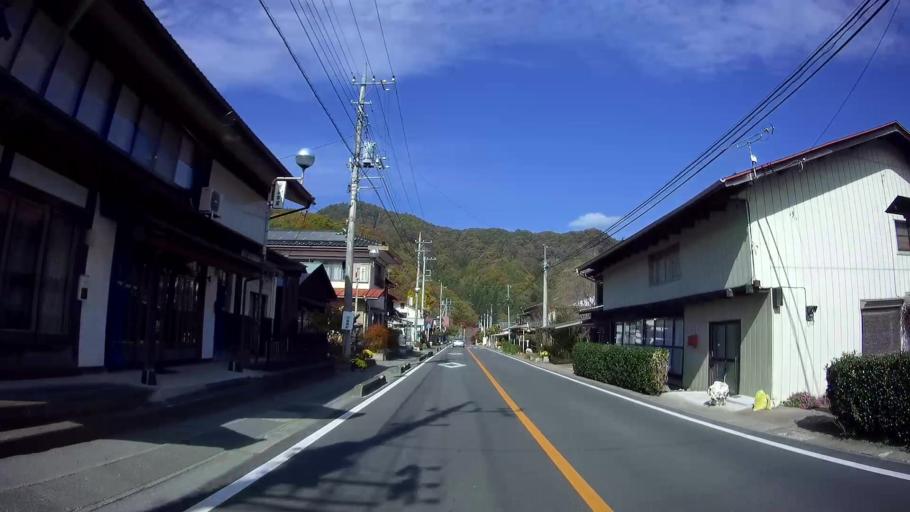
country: JP
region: Gunma
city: Nakanojomachi
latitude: 36.5105
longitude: 138.7752
